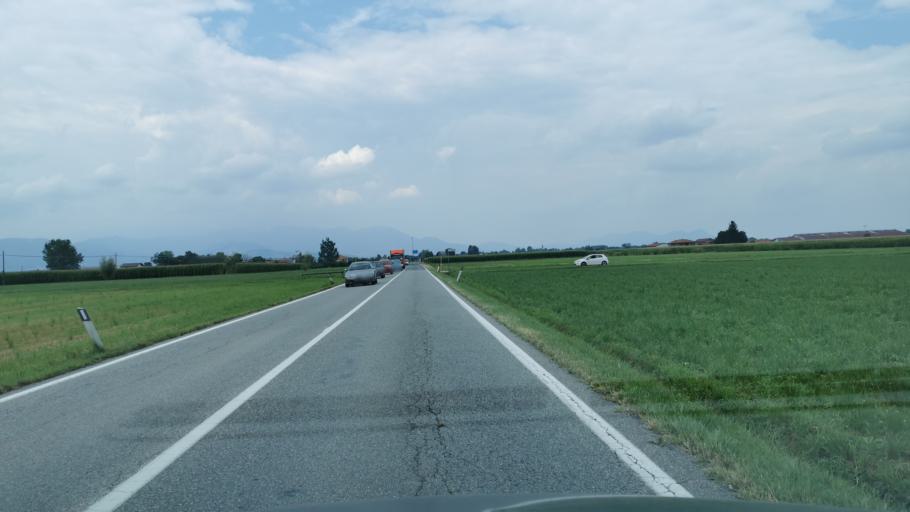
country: IT
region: Piedmont
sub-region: Provincia di Torino
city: Cavour
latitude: 44.8112
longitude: 7.3720
